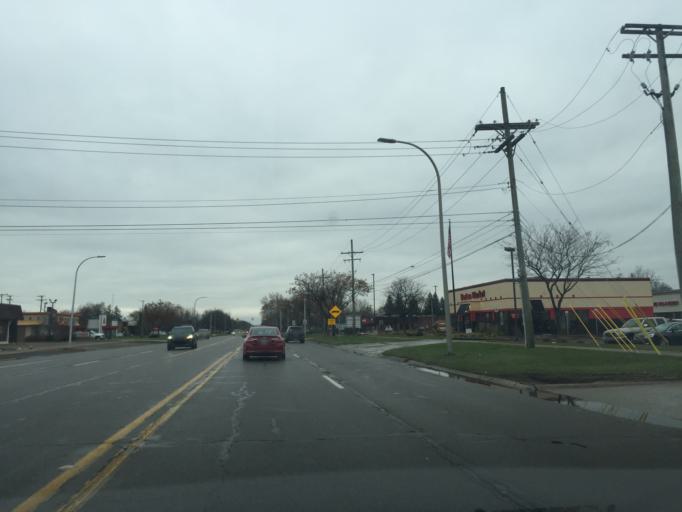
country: US
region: Michigan
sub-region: Oakland County
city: Farmington
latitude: 42.4268
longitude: -83.3359
